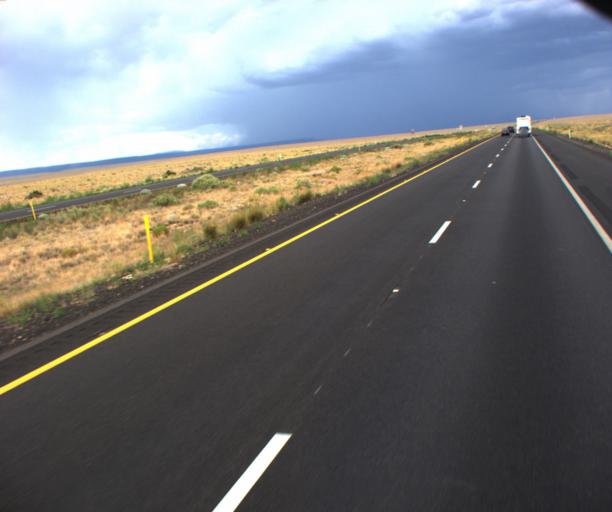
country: US
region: Arizona
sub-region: Coconino County
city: LeChee
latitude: 35.1180
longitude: -111.1262
